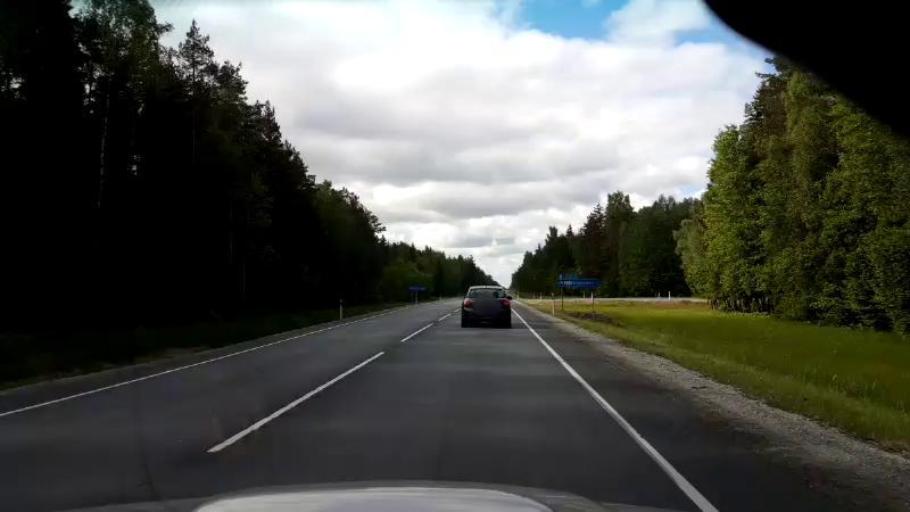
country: EE
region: Raplamaa
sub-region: Maerjamaa vald
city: Marjamaa
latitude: 58.8849
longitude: 24.4511
